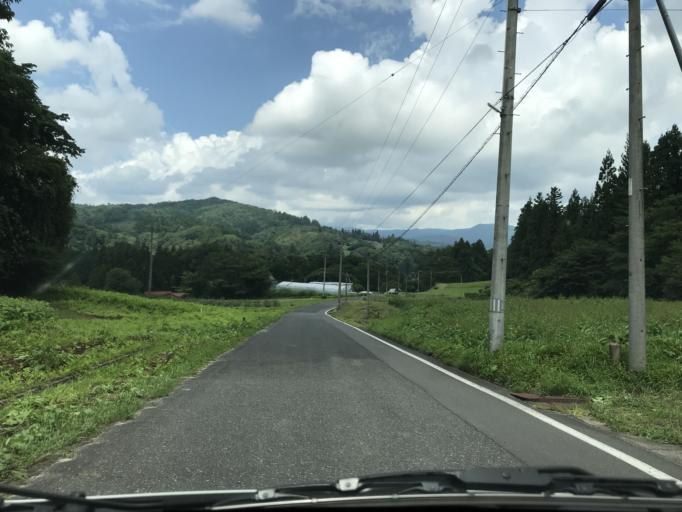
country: JP
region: Iwate
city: Mizusawa
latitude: 39.0379
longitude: 141.3515
